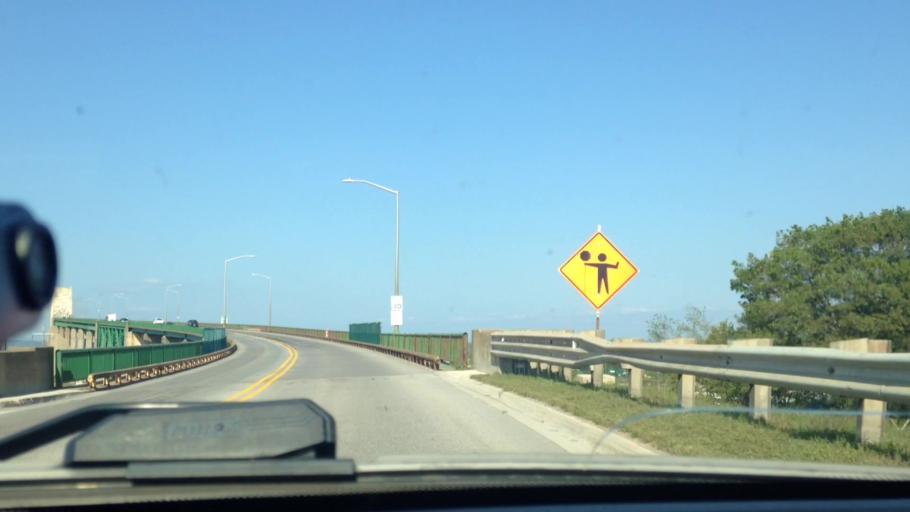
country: US
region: Michigan
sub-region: Chippewa County
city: Sault Ste. Marie
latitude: 46.4957
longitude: -84.3663
